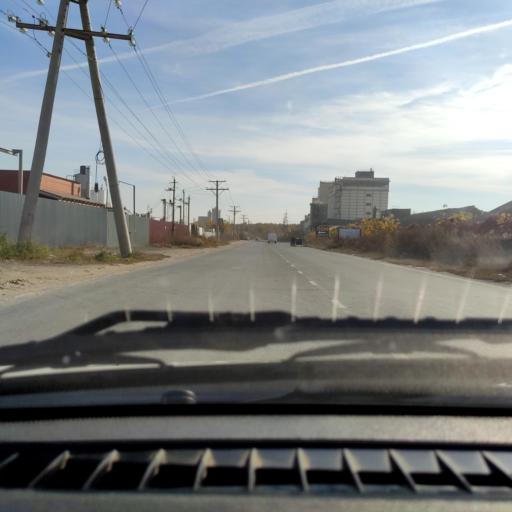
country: RU
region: Samara
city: Zhigulevsk
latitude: 53.5259
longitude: 49.4826
